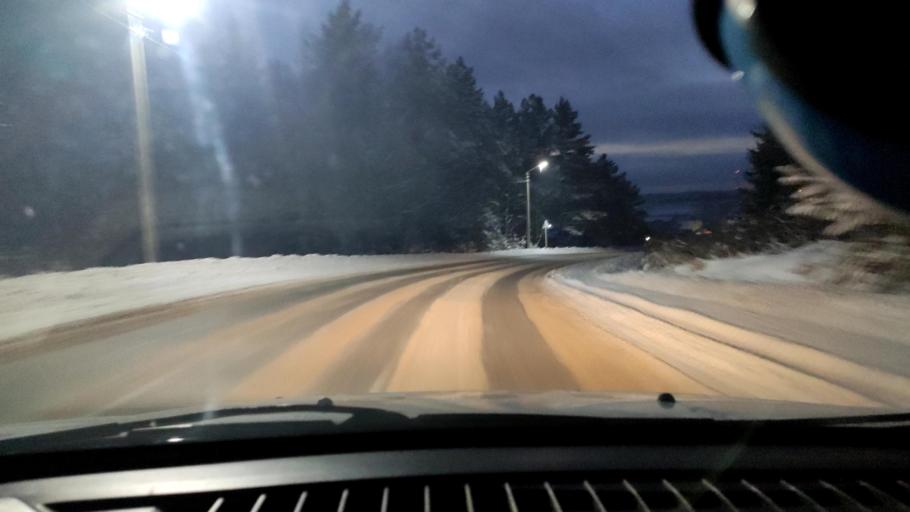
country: RU
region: Perm
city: Kultayevo
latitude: 57.9122
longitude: 55.9055
